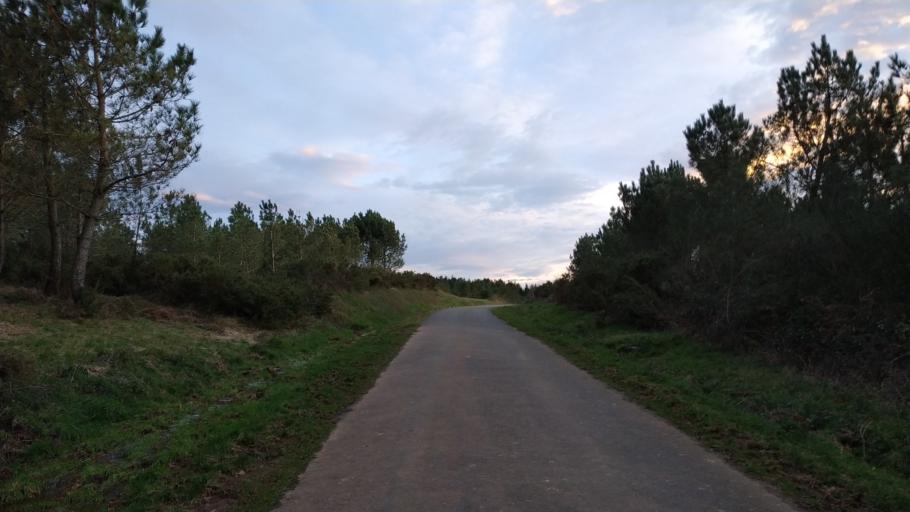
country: ES
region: Galicia
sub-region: Provincia de Pontevedra
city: Silleda
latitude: 42.7670
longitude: -8.1612
